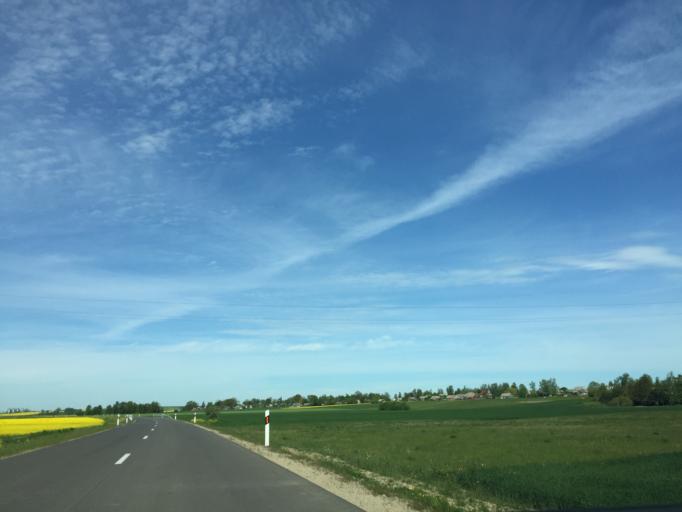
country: LT
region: Panevezys
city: Pasvalys
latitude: 56.1137
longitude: 24.2298
